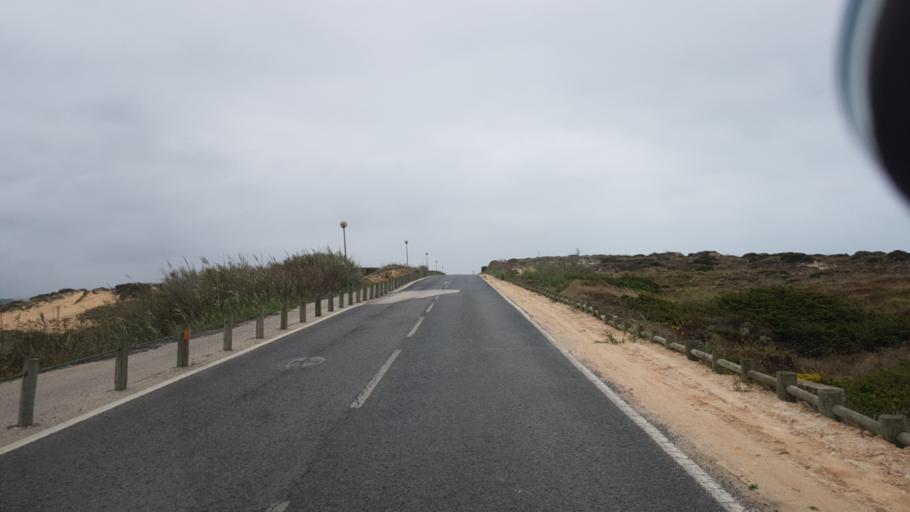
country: PT
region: Lisbon
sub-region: Torres Vedras
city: Silveira
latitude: 39.1671
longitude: -9.3584
